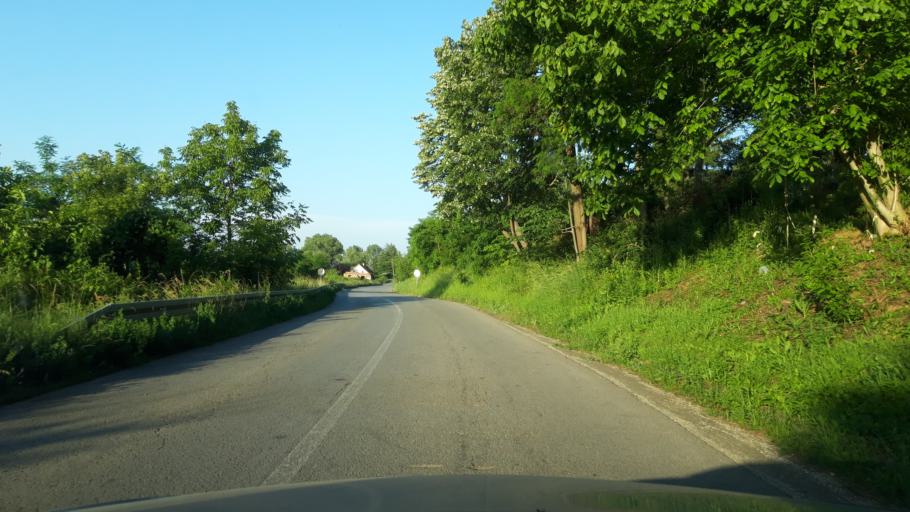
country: RS
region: Autonomna Pokrajina Vojvodina
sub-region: Juznobacki Okrug
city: Beocin
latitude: 45.2192
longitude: 19.6478
